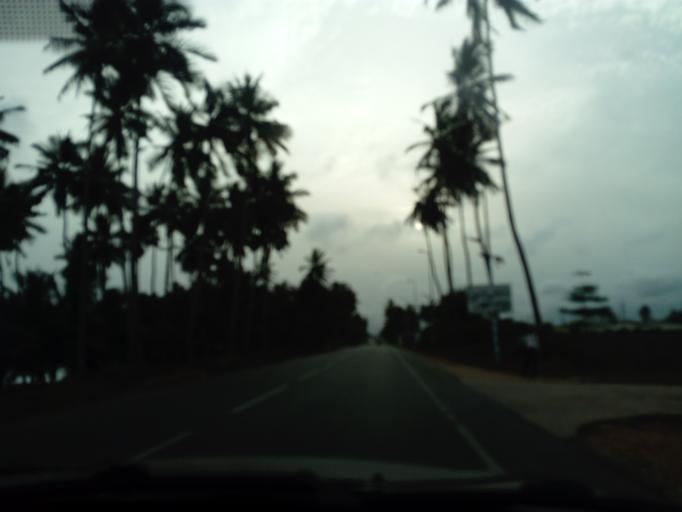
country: GH
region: Central
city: Cape Coast
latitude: 5.1012
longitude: -1.2745
